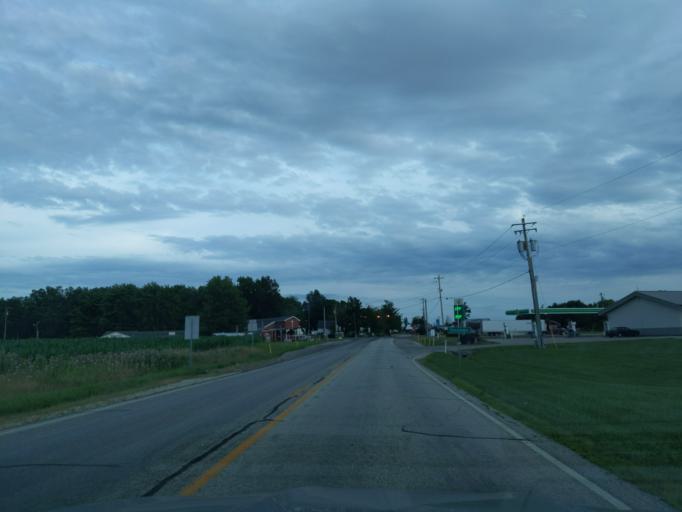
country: US
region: Indiana
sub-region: Ripley County
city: Sunman
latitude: 39.2733
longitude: -85.0977
